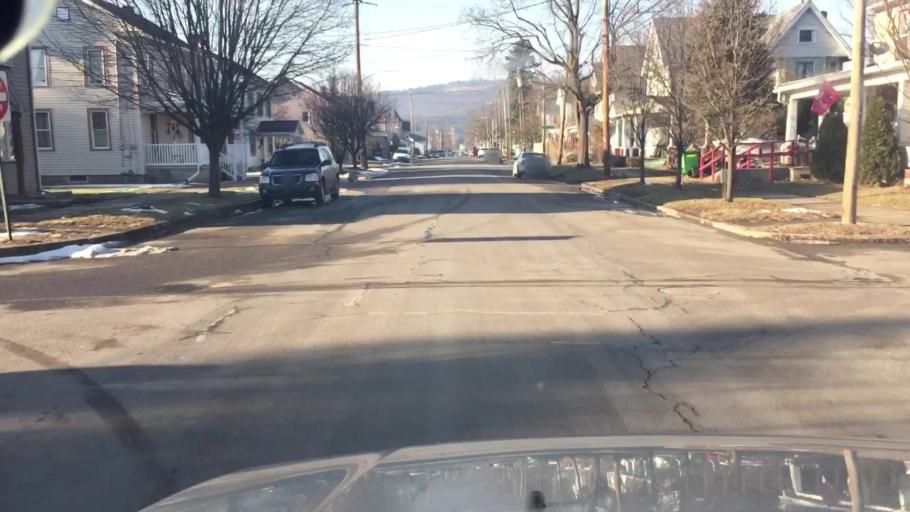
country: US
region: Pennsylvania
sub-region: Columbia County
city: Berwick
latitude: 41.0581
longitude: -76.2315
